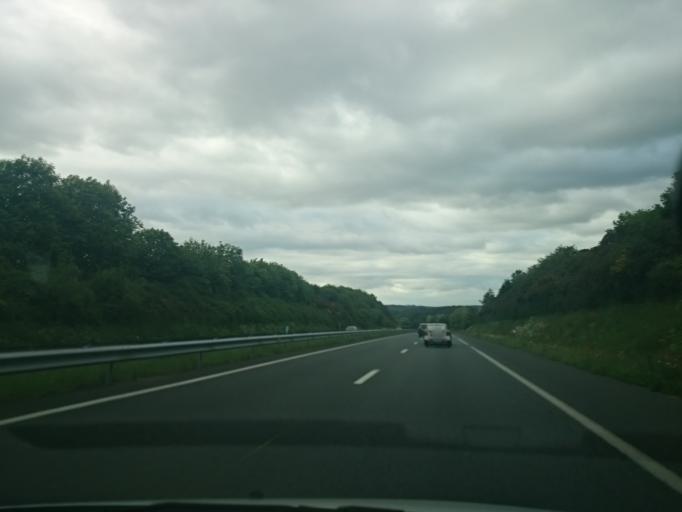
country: FR
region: Brittany
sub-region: Departement du Morbihan
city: Nivillac
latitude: 47.5245
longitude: -2.2828
